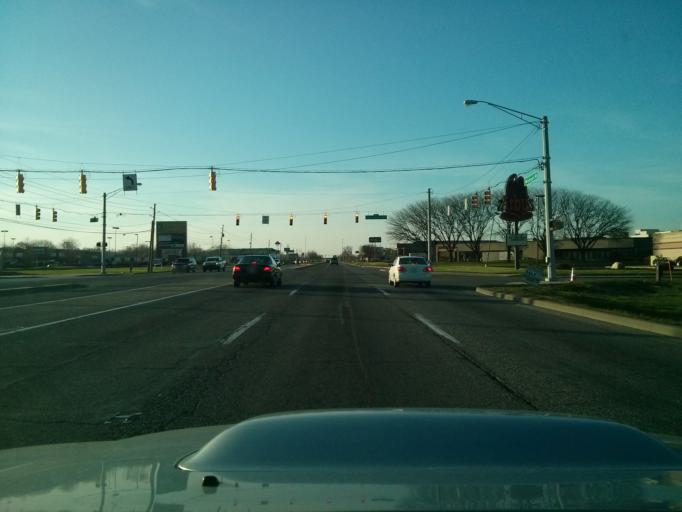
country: US
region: Indiana
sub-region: Boone County
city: Zionsville
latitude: 39.9149
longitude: -86.2241
